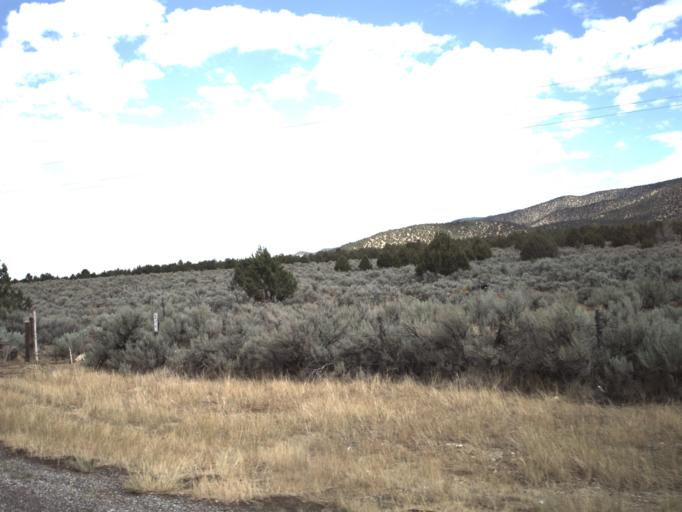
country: US
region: Utah
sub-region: Sanpete County
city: Gunnison
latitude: 39.1942
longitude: -112.0803
